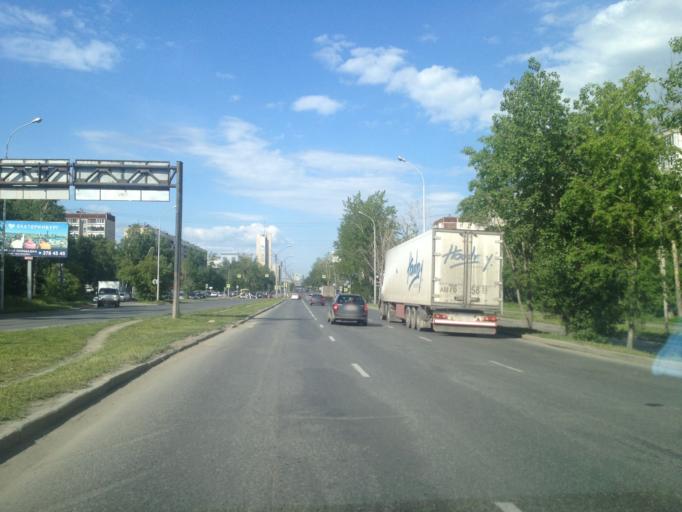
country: RU
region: Sverdlovsk
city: Sovkhoznyy
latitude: 56.8060
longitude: 60.5415
